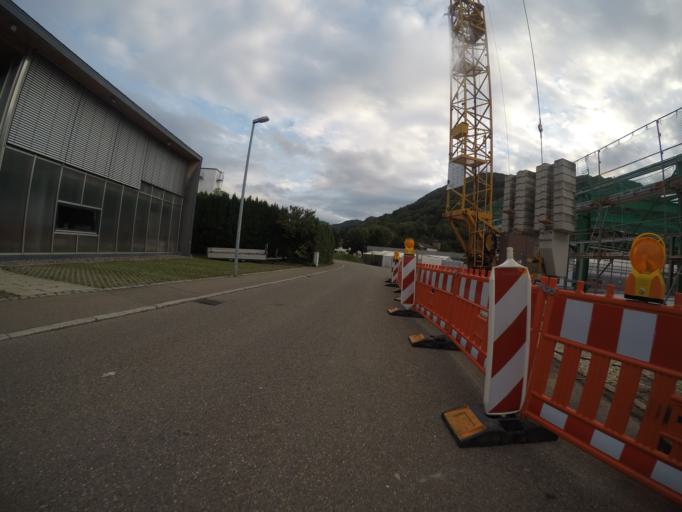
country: DE
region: Baden-Wuerttemberg
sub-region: Tuebingen Region
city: Pfullingen
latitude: 48.4417
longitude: 9.2543
